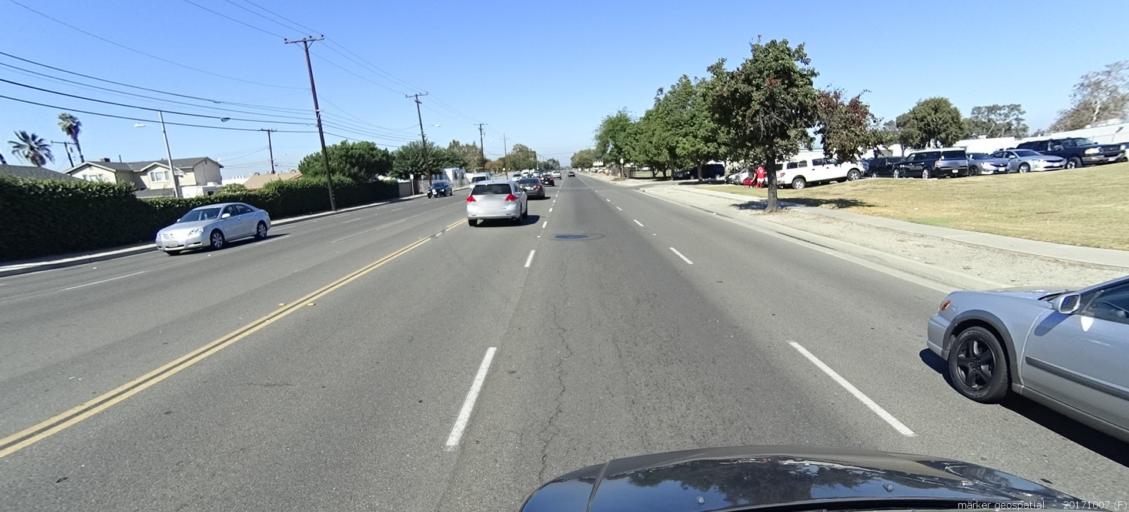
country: US
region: California
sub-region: Orange County
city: Stanton
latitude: 33.7892
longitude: -118.0111
